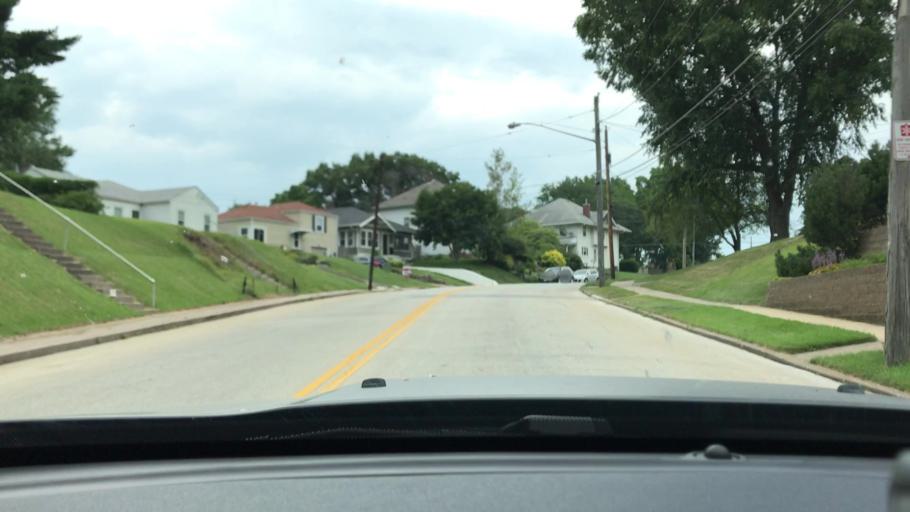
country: US
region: Iowa
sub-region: Scott County
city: Bettendorf
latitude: 41.5353
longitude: -90.5394
